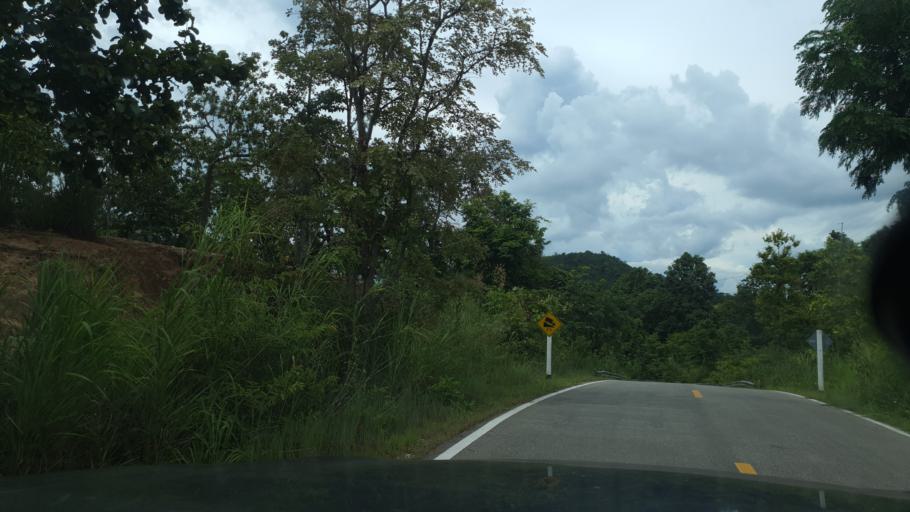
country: TH
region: Lamphun
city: Mae Tha
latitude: 18.5201
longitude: 99.2633
